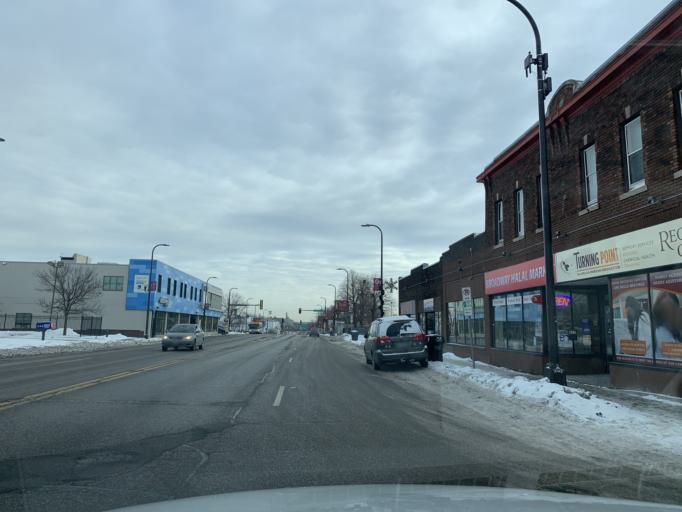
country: US
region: Minnesota
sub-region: Hennepin County
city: Minneapolis
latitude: 44.9991
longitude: -93.2902
